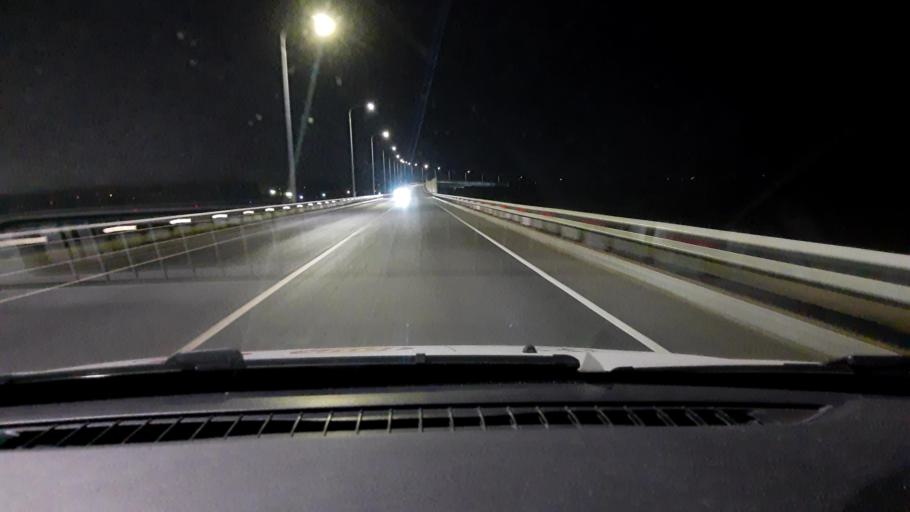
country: RU
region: Nizjnij Novgorod
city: Neklyudovo
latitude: 56.4125
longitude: 43.9834
